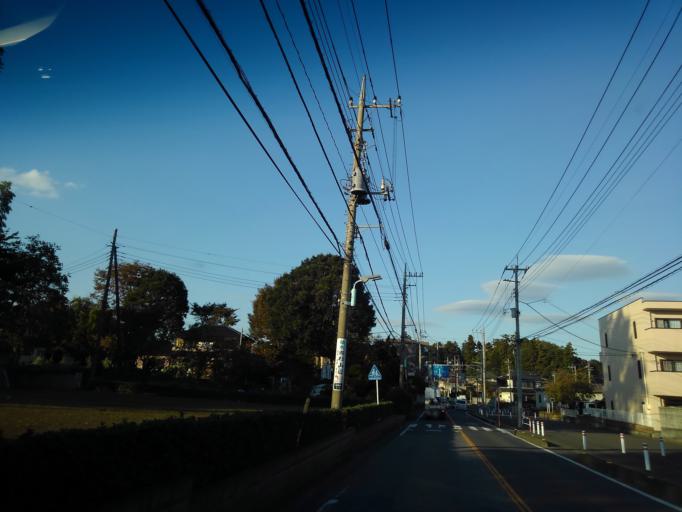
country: JP
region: Saitama
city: Tokorozawa
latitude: 35.7875
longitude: 139.4275
